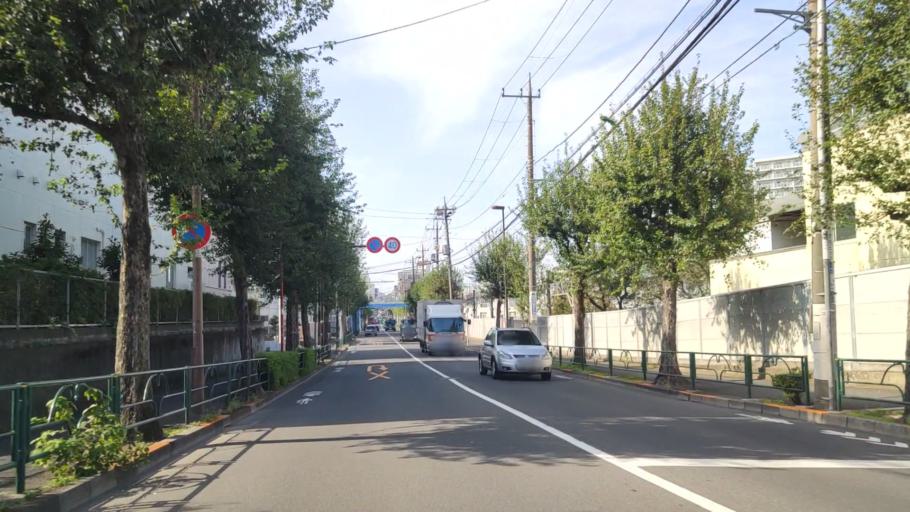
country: JP
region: Tokyo
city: Tokyo
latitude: 35.6856
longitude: 139.6652
